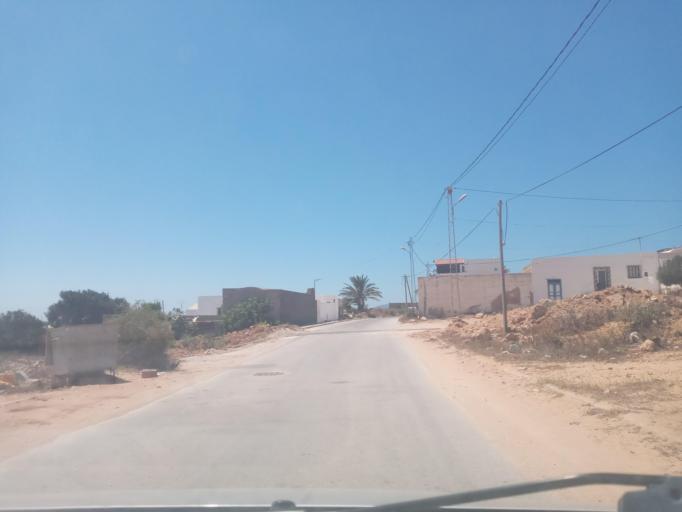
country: TN
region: Nabul
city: El Haouaria
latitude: 37.0509
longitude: 11.0003
